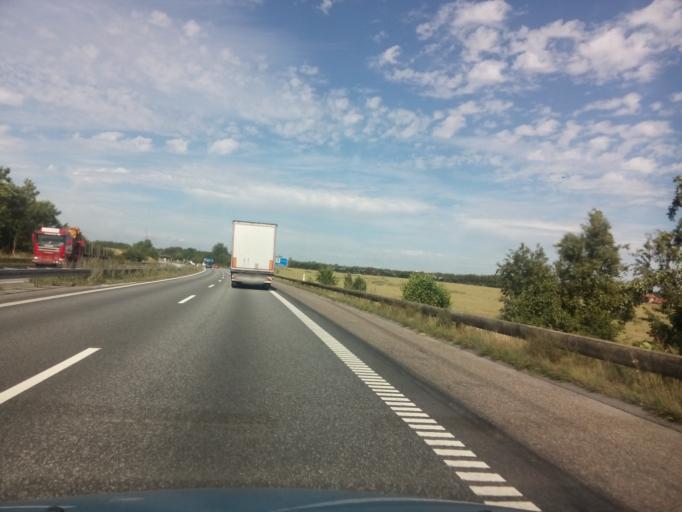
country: DK
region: Central Jutland
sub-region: Randers Kommune
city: Randers
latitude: 56.4197
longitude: 10.0683
